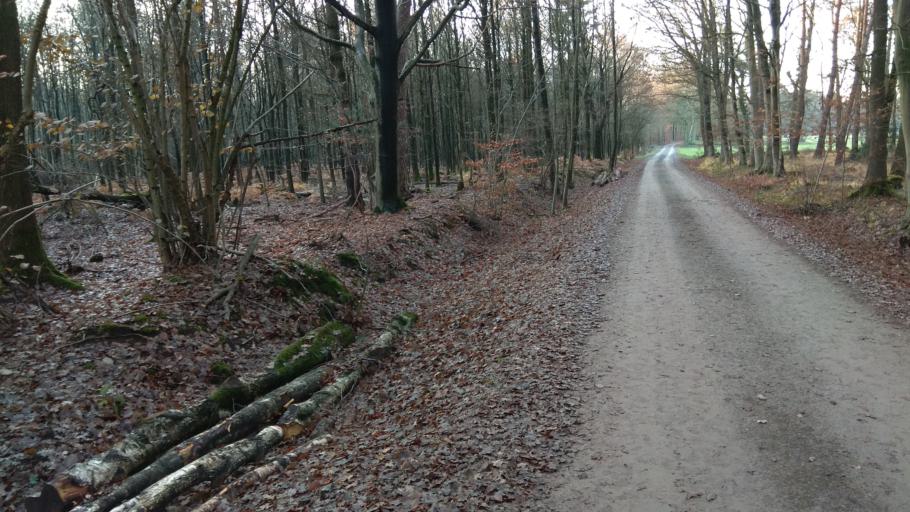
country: DE
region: North Rhine-Westphalia
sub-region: Regierungsbezirk Dusseldorf
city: Schermbeck
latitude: 51.6410
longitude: 6.8612
